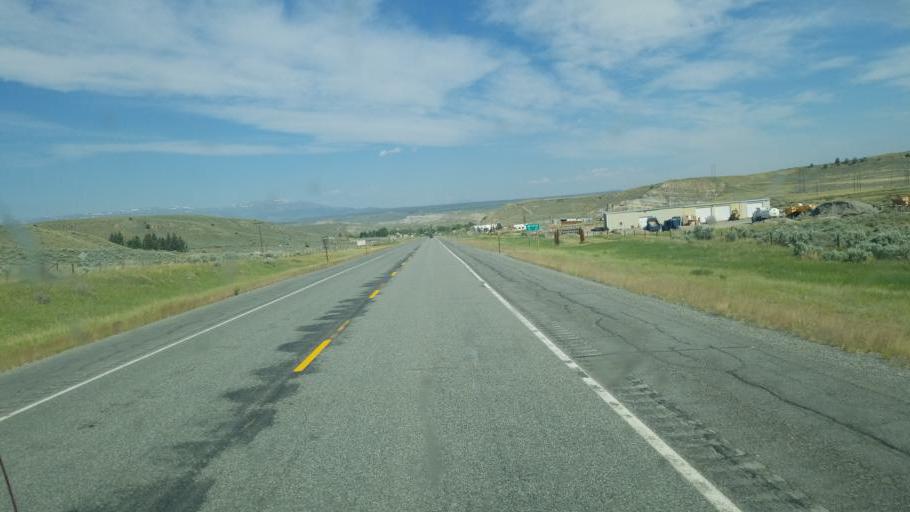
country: US
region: Wyoming
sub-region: Park County
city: Cody
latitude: 44.1495
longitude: -108.8550
